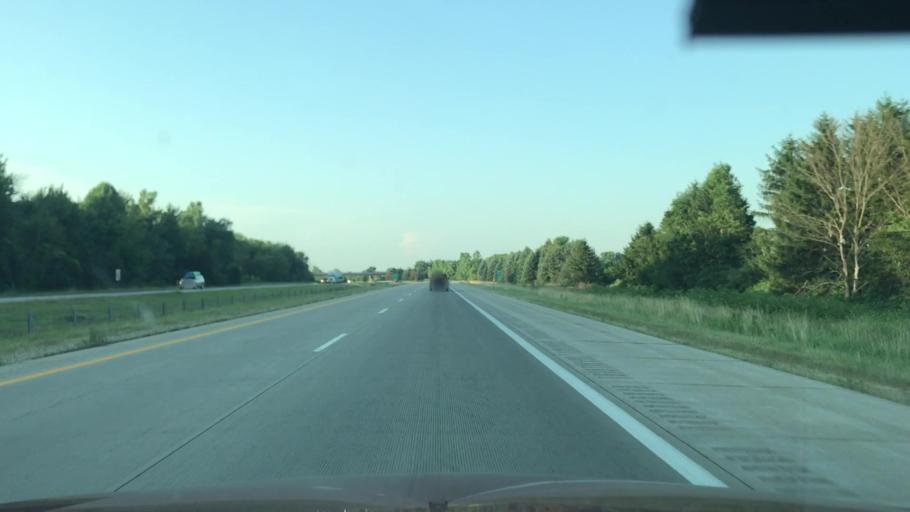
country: US
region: Michigan
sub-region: Van Buren County
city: South Haven
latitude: 42.4649
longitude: -86.2266
